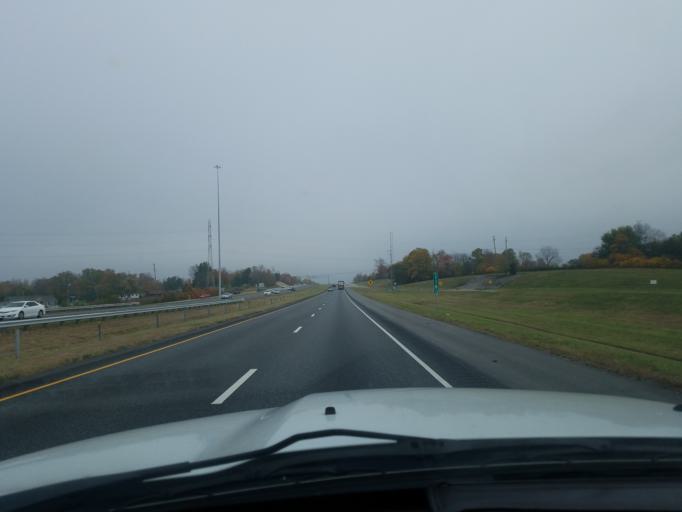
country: US
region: Indiana
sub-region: Floyd County
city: Georgetown
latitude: 38.2876
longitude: -85.9114
